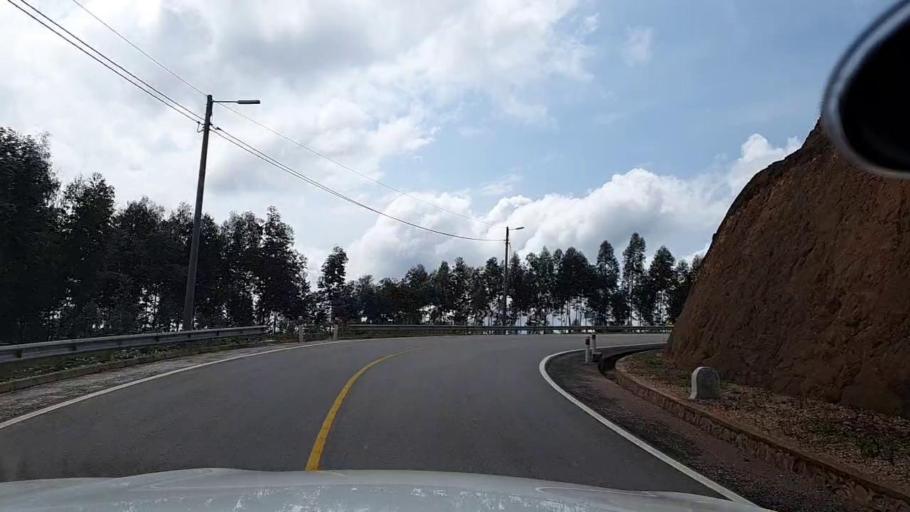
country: RW
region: Southern Province
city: Nzega
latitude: -2.5198
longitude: 29.4590
